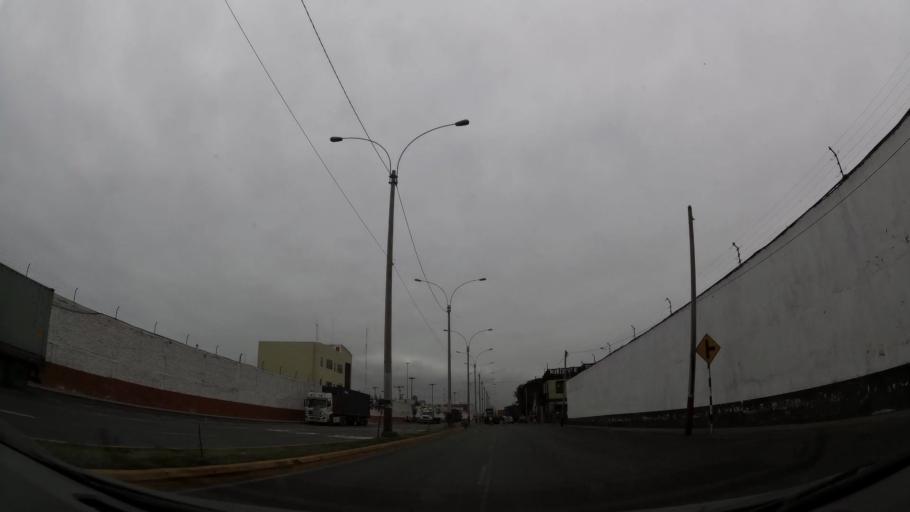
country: PE
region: Callao
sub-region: Callao
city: Callao
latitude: -12.0548
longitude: -77.1430
